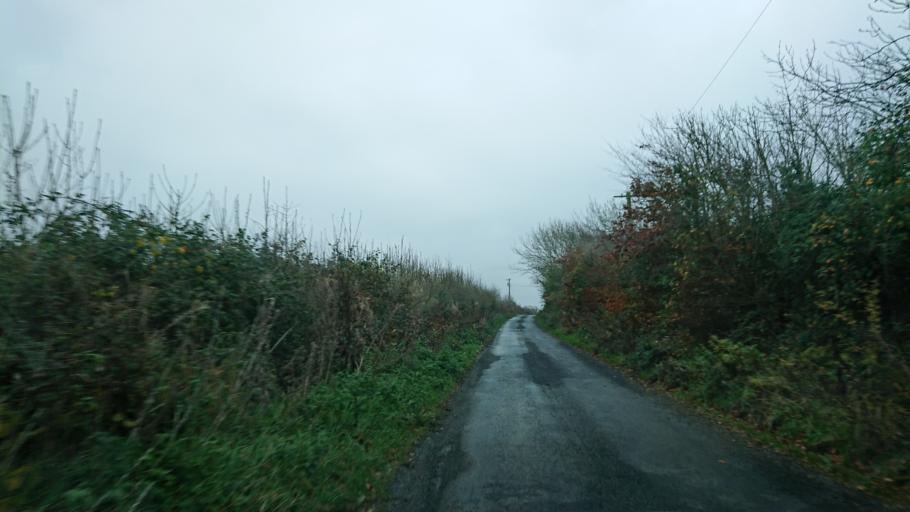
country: IE
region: Munster
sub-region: Waterford
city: Dunmore East
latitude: 52.1983
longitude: -7.0078
